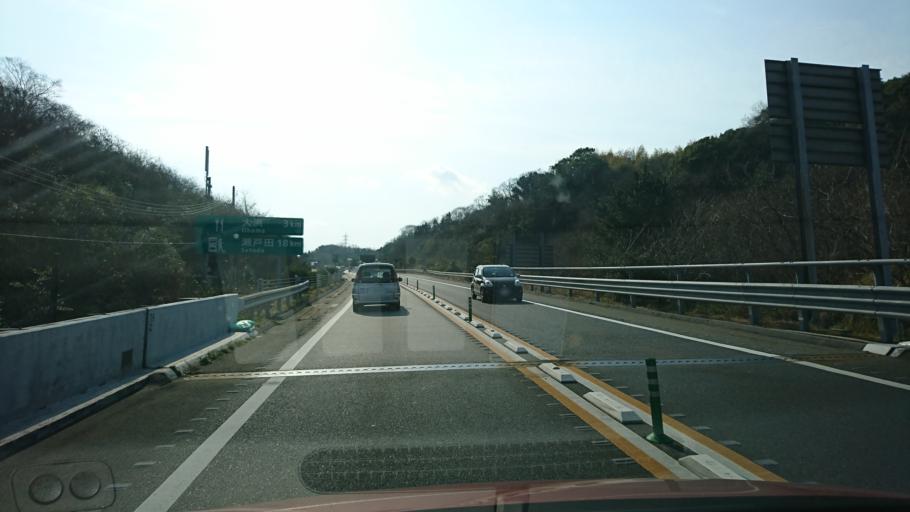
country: JP
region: Hiroshima
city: Onomichi
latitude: 34.3703
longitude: 133.1904
